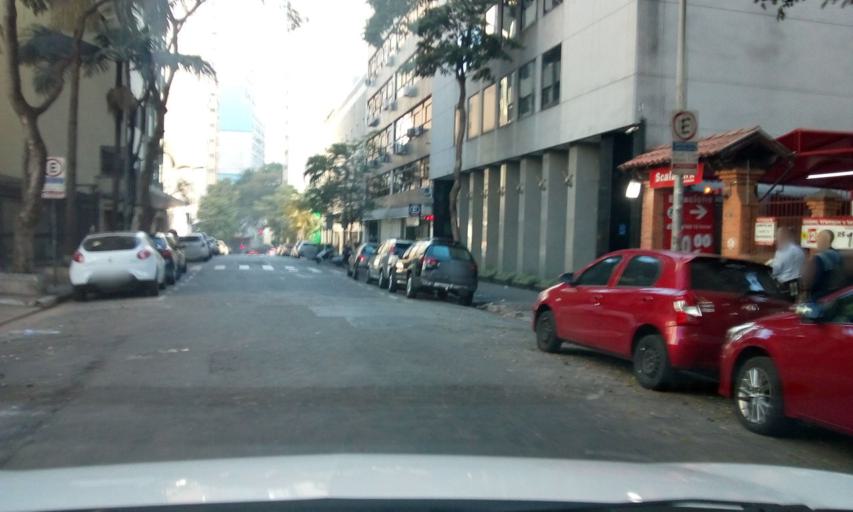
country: BR
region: Sao Paulo
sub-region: Sao Paulo
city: Sao Paulo
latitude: -23.5493
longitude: -46.6455
